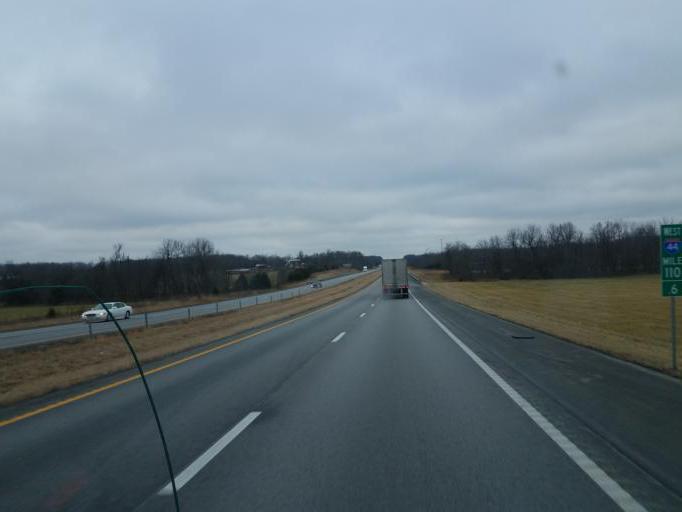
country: US
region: Missouri
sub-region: Webster County
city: Marshfield
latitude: 37.4684
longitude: -92.8601
